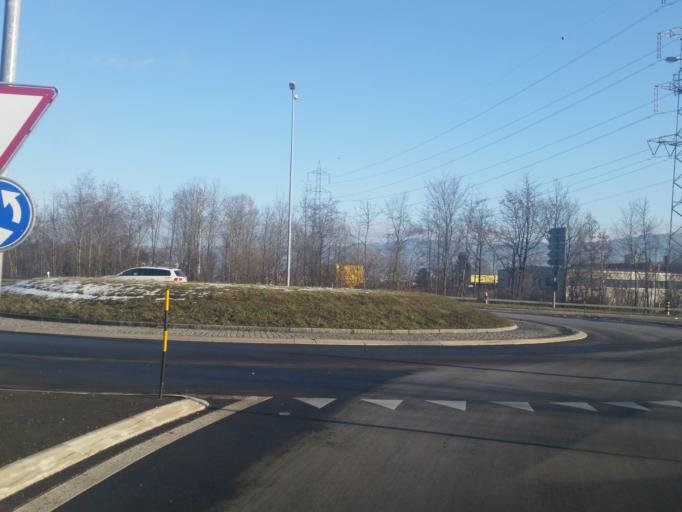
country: CH
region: Zug
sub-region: Zug
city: Cham
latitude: 47.1911
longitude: 8.4717
